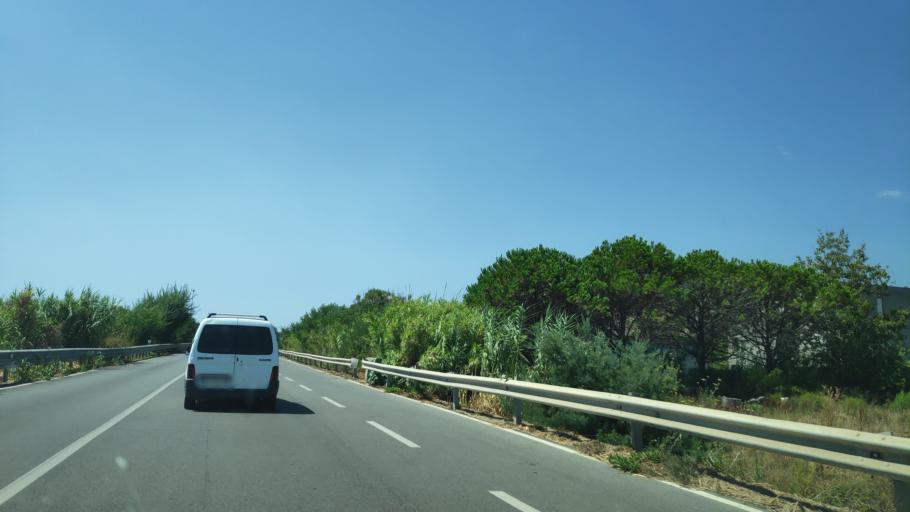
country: IT
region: Calabria
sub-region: Provincia di Reggio Calabria
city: Brancaleone-Marina
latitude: 37.9838
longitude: 16.1162
